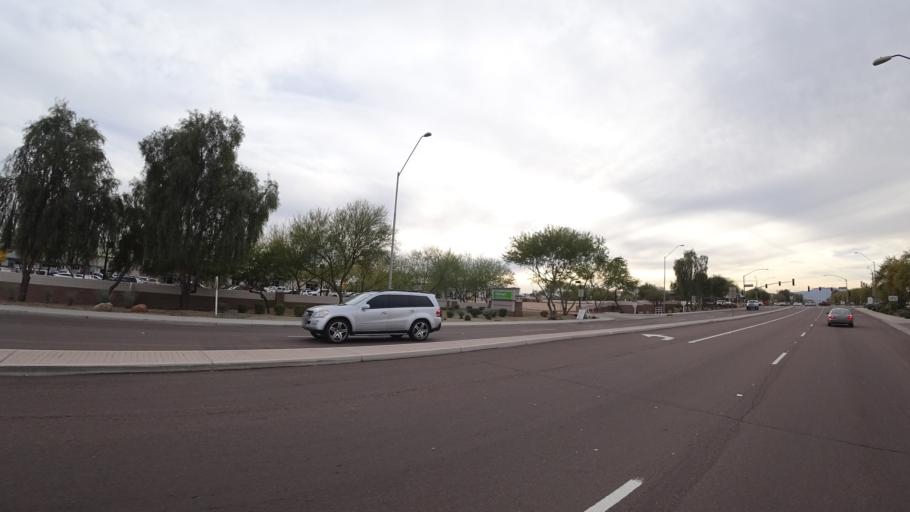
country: US
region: Arizona
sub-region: Maricopa County
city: Surprise
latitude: 33.6241
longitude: -112.3924
